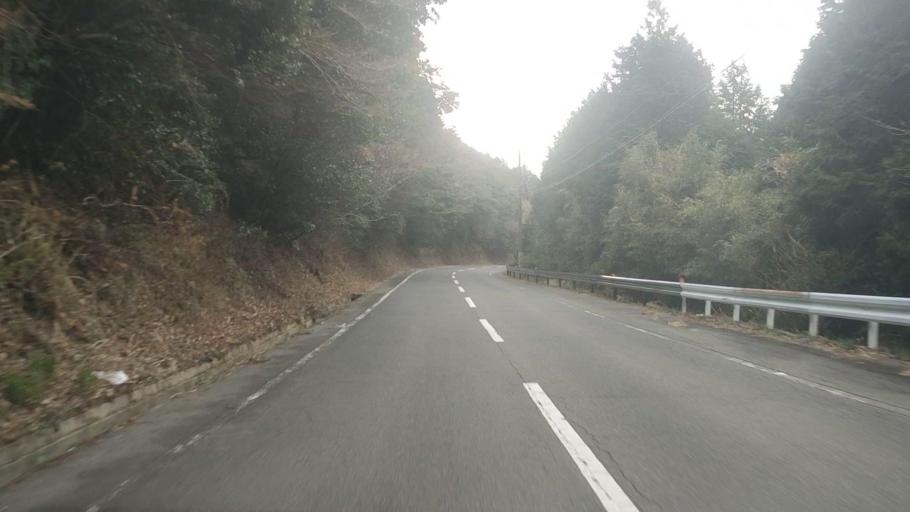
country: JP
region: Nagasaki
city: Shimabara
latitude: 32.7232
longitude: 130.2497
